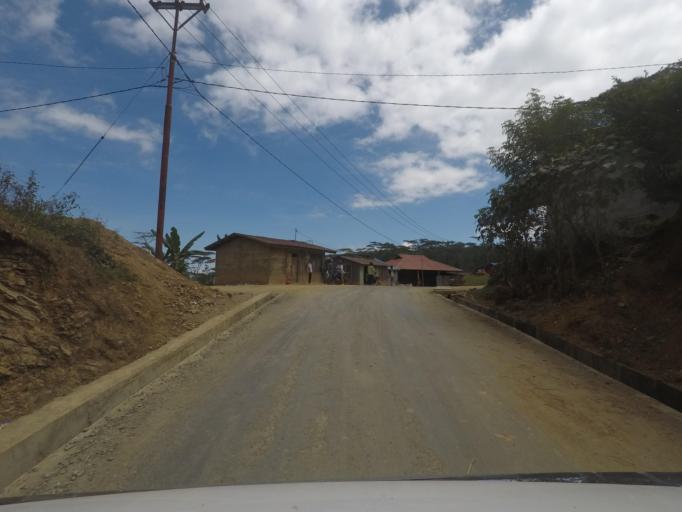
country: TL
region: Ermera
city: Gleno
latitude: -8.7474
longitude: 125.3511
